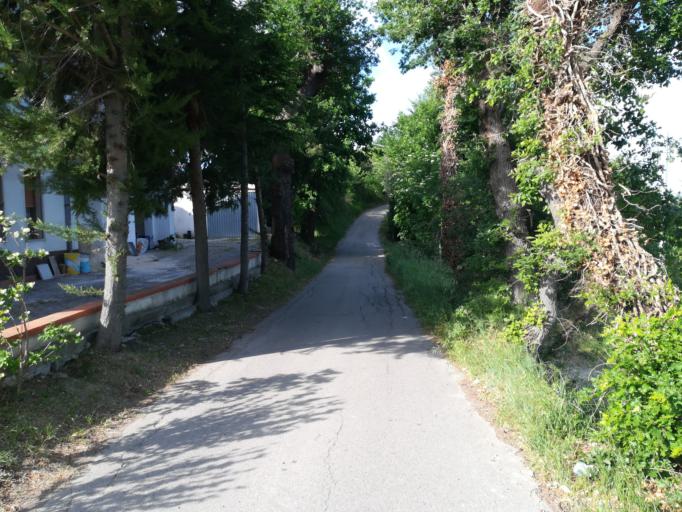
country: IT
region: Abruzzo
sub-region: Provincia di Chieti
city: Bucchianico
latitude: 42.2954
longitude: 14.1698
